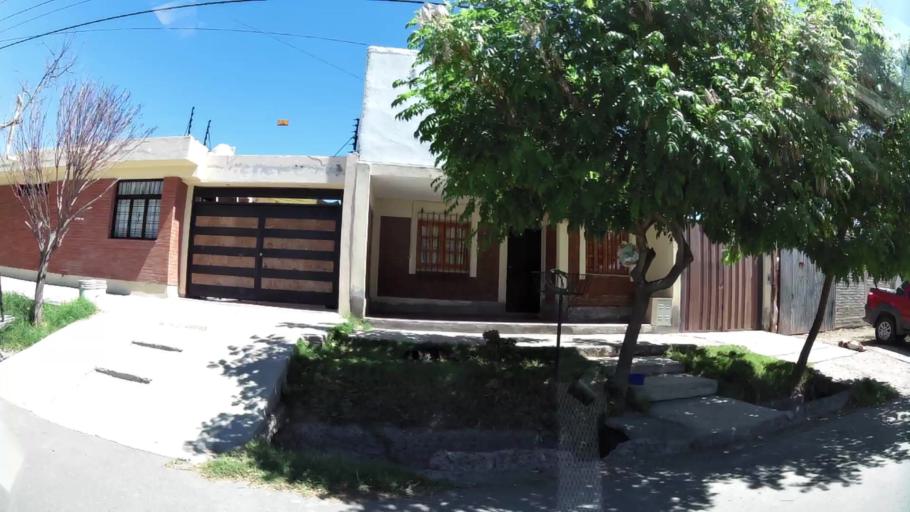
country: AR
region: Mendoza
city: Las Heras
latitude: -32.8362
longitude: -68.8725
